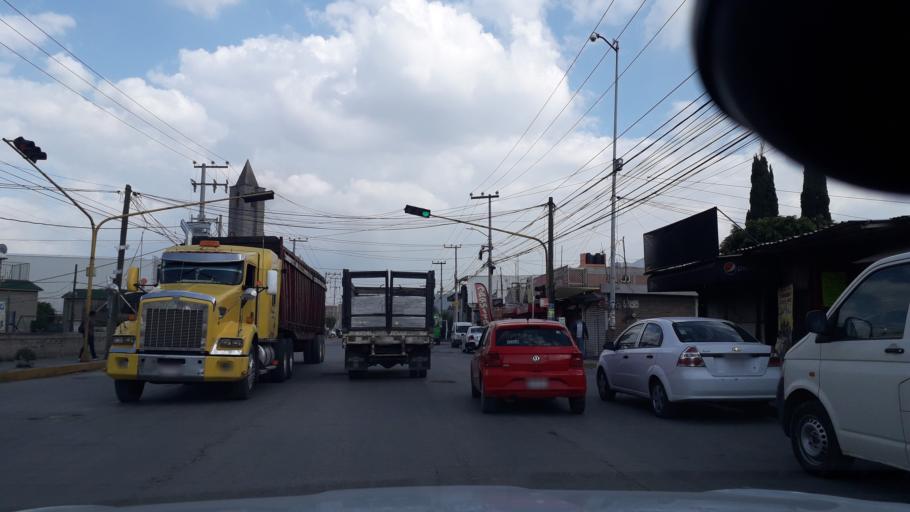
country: MX
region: Mexico
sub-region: Tultitlan
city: Colonia Lazaro Cardenas (Los Hornos)
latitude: 19.6308
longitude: -99.1701
